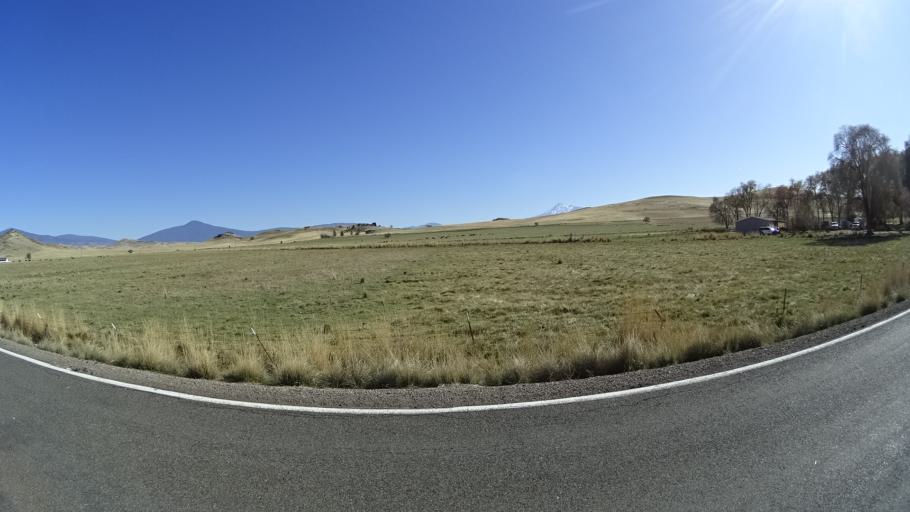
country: US
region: California
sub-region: Siskiyou County
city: Montague
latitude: 41.7464
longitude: -122.5054
